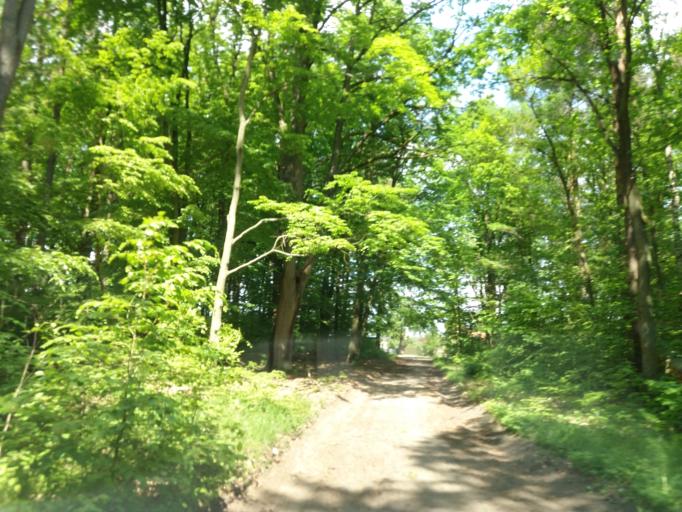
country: PL
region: West Pomeranian Voivodeship
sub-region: Powiat choszczenski
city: Bierzwnik
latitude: 53.0285
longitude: 15.6663
